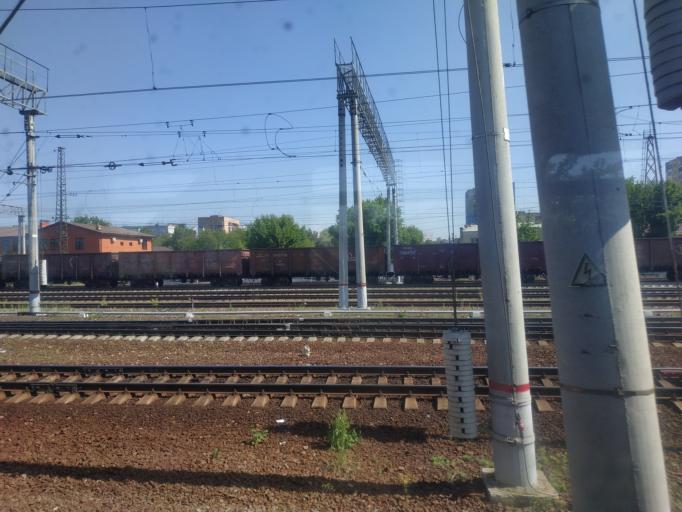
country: RU
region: Moskovskaya
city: Ramenskoye
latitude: 55.5628
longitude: 38.2321
